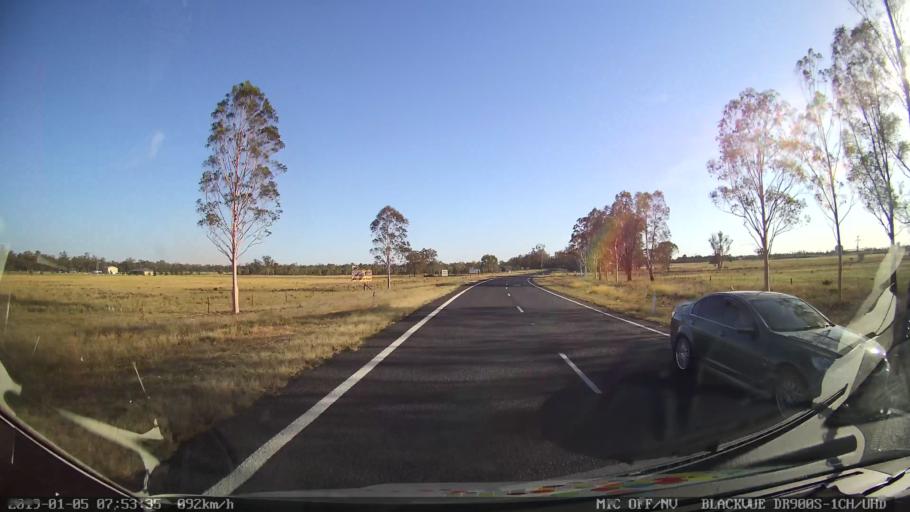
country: AU
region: New South Wales
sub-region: Gilgandra
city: Gilgandra
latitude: -31.7422
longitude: 148.6424
